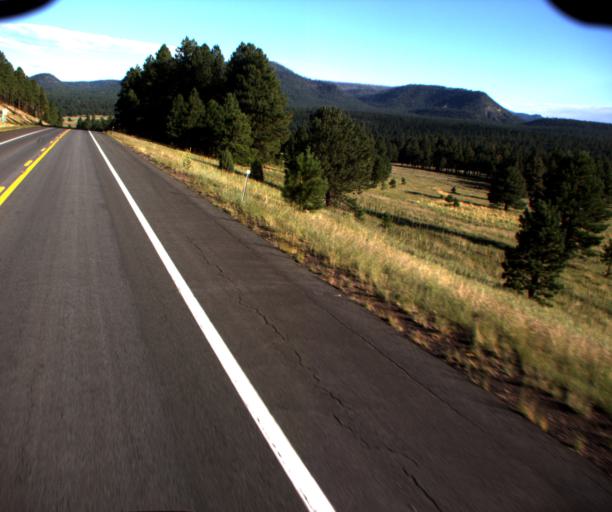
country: US
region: New Mexico
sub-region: Catron County
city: Reserve
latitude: 33.8221
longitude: -109.0774
